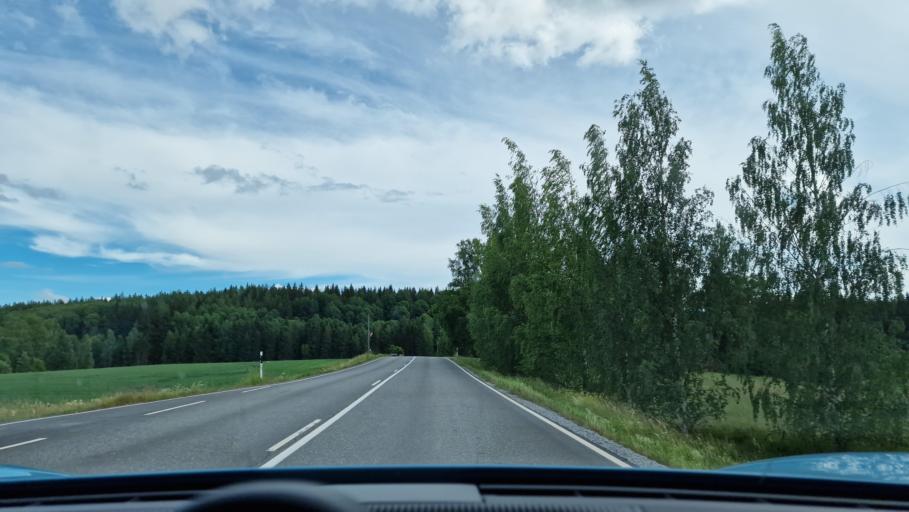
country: FI
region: Pirkanmaa
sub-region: Tampere
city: Orivesi
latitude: 61.6039
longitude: 24.3107
